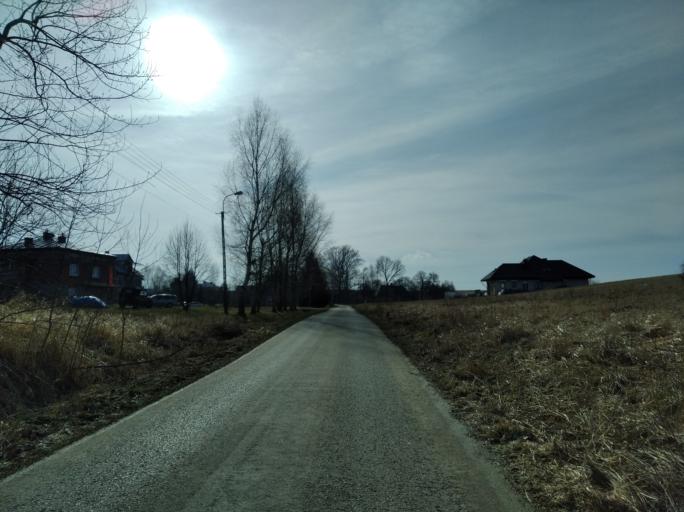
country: PL
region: Subcarpathian Voivodeship
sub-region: Powiat brzozowski
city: Humniska
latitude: 49.6628
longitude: 22.0515
